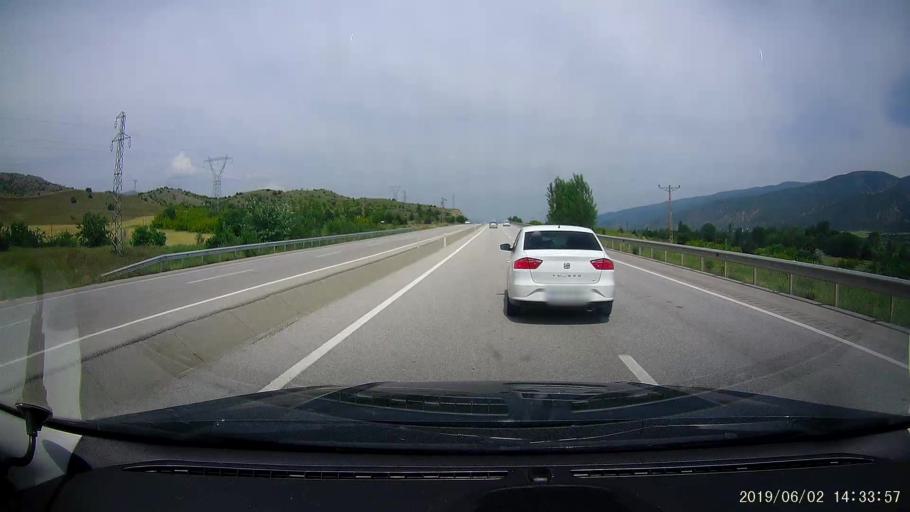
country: TR
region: Kastamonu
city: Tosya
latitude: 41.0346
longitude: 34.1819
